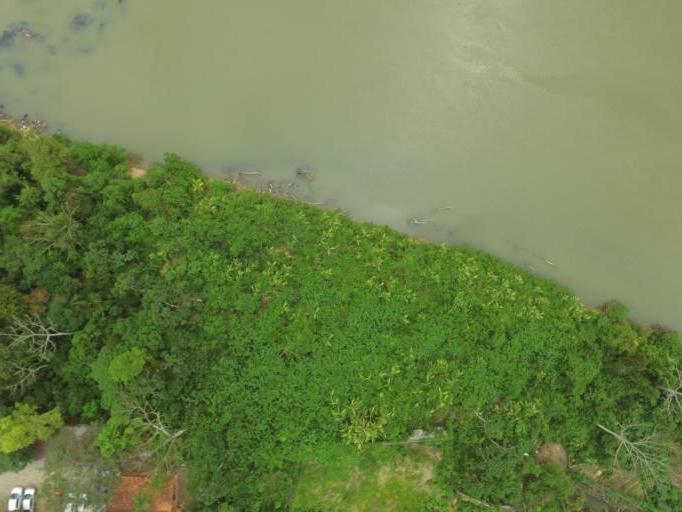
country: BR
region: Santa Catarina
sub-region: Blumenau
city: Blumenau
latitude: -26.8905
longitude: -49.1322
